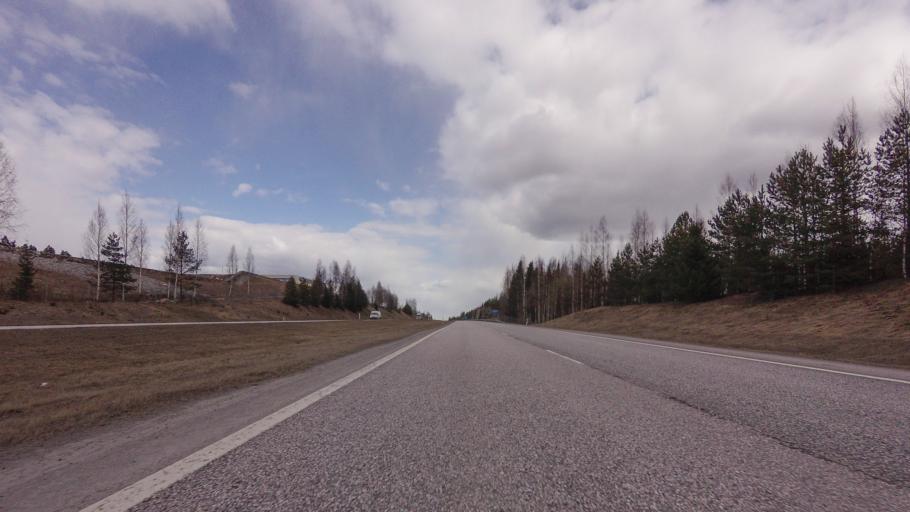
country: FI
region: Uusimaa
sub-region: Helsinki
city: Nurmijaervi
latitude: 60.4419
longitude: 24.8381
